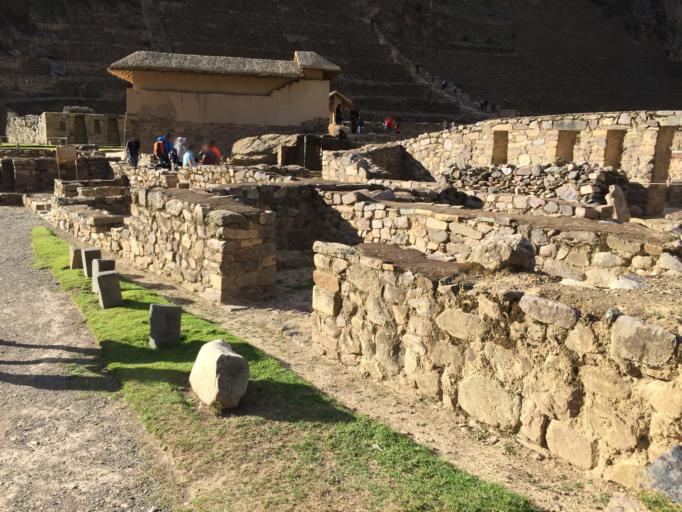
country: PE
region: Cusco
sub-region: Provincia de Urubamba
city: Ollantaytambo
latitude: -13.2571
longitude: -72.2652
